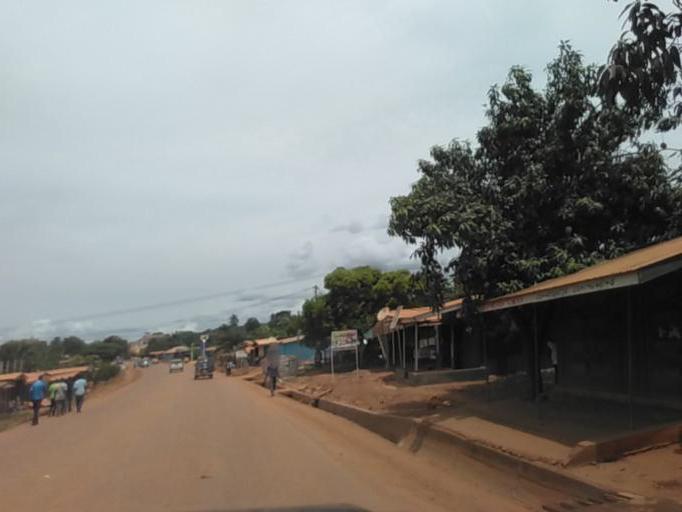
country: GH
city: Akropong
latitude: 6.1254
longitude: -0.0010
